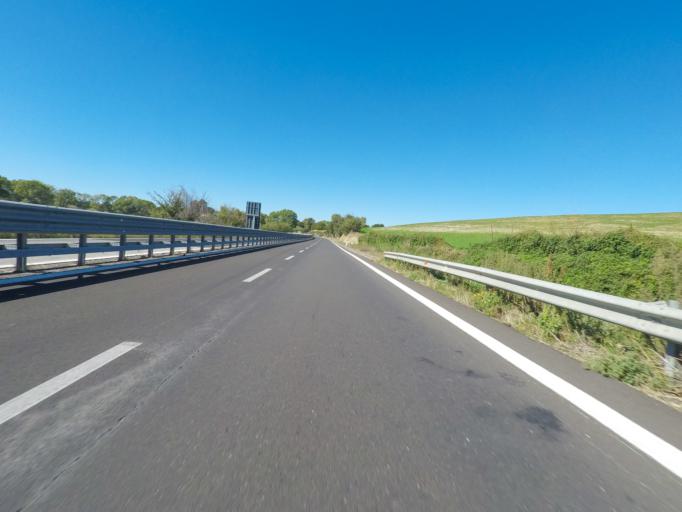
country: IT
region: Latium
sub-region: Provincia di Viterbo
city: Montalto di Castro
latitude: 42.3188
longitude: 11.6512
